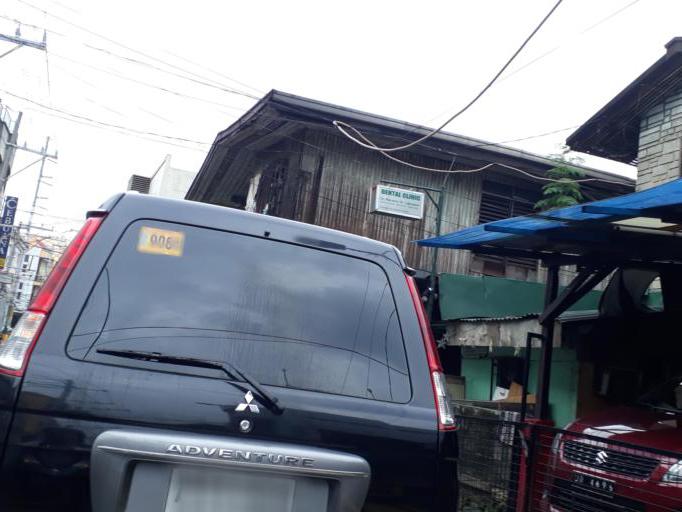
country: PH
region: Metro Manila
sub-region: City of Manila
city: Manila
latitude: 14.6333
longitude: 120.9795
